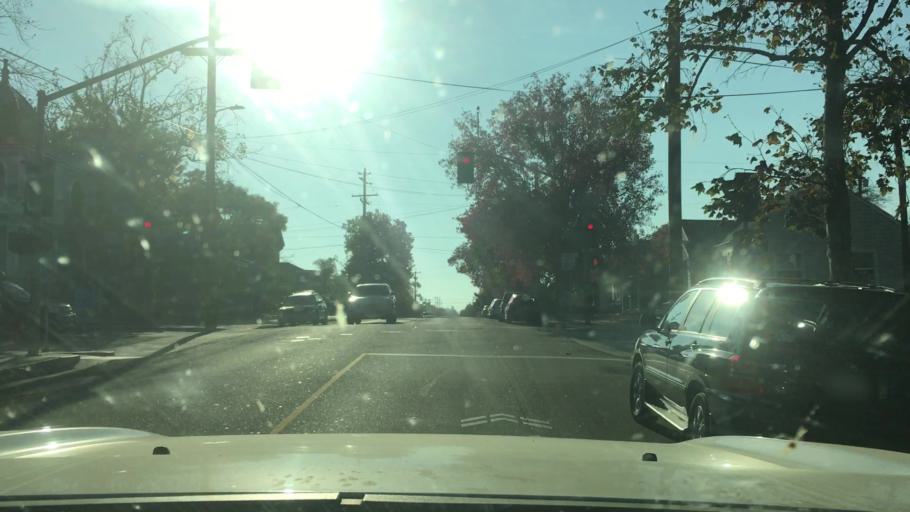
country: US
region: California
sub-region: San Luis Obispo County
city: San Luis Obispo
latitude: 35.2760
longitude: -120.6619
